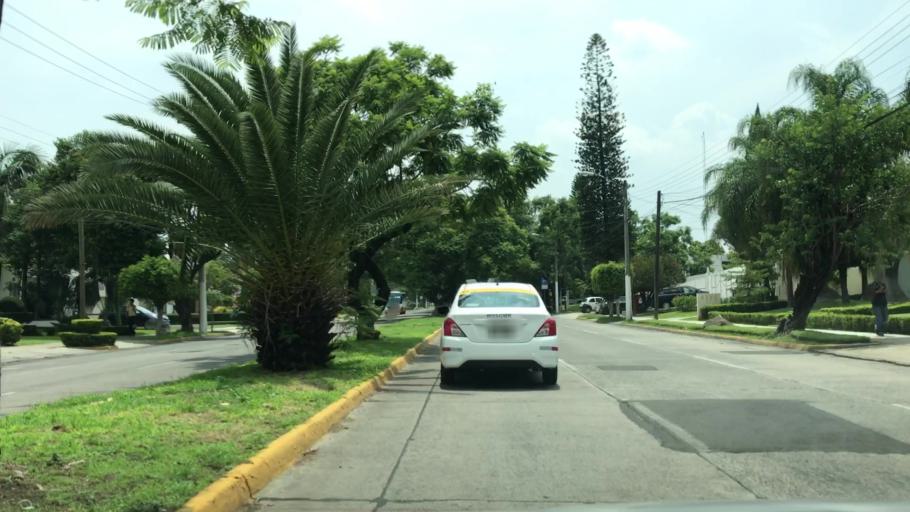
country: MX
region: Jalisco
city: Guadalajara
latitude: 20.6507
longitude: -103.4131
